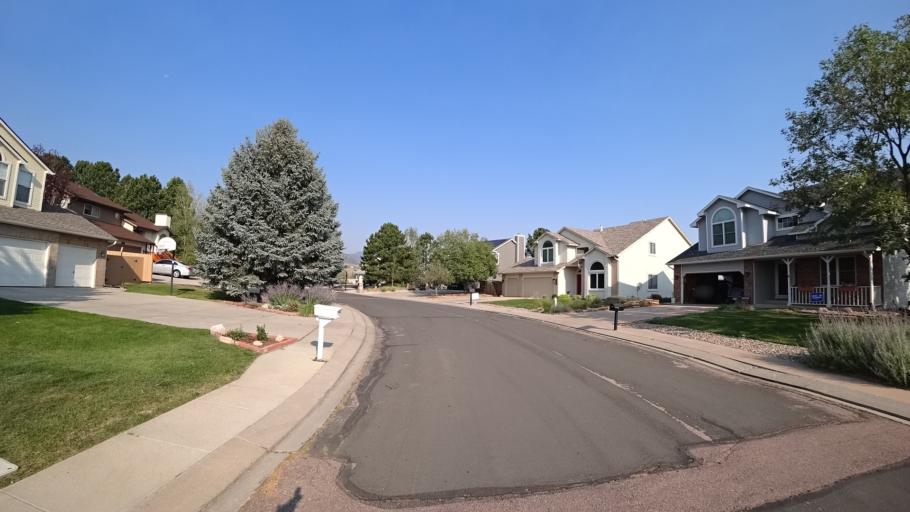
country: US
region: Colorado
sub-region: El Paso County
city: Colorado Springs
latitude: 38.8157
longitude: -104.8463
